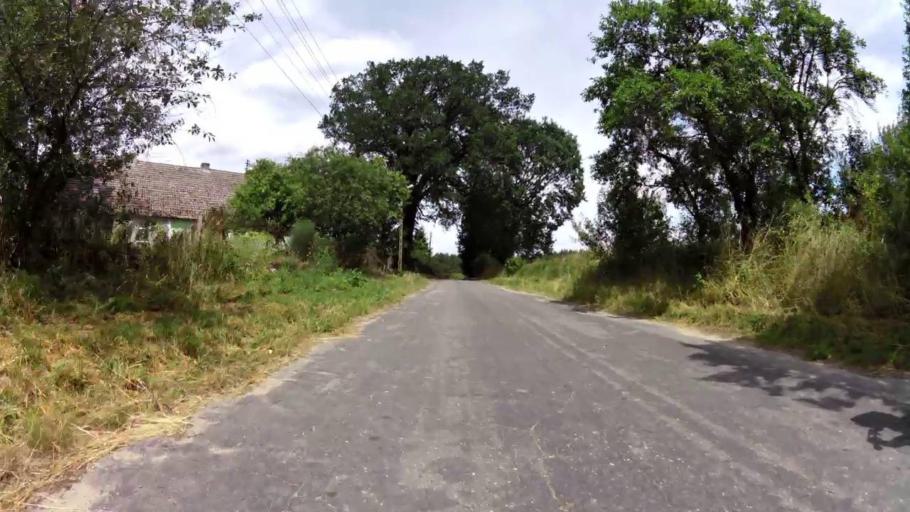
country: PL
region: West Pomeranian Voivodeship
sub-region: Powiat lobeski
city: Lobez
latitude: 53.5408
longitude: 15.6765
